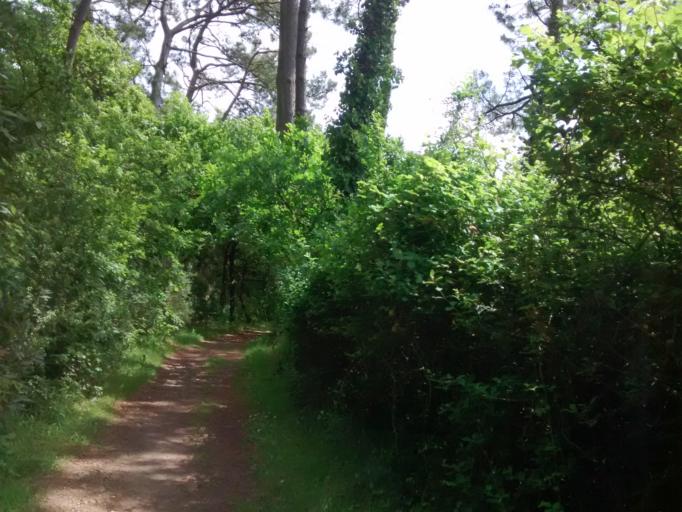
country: FR
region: Brittany
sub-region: Departement du Morbihan
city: Larmor-Baden
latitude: 47.5979
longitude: -2.8946
